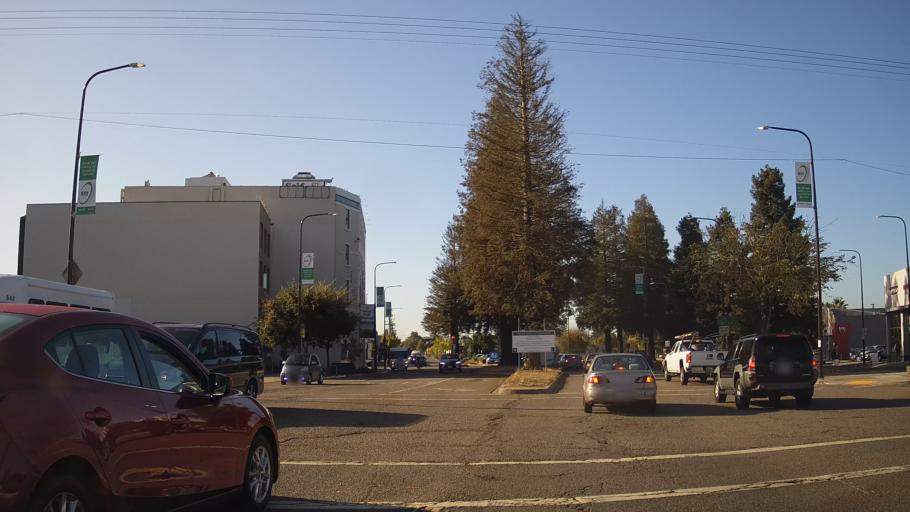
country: US
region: California
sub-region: Alameda County
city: Berkeley
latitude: 37.8605
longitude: -122.2671
